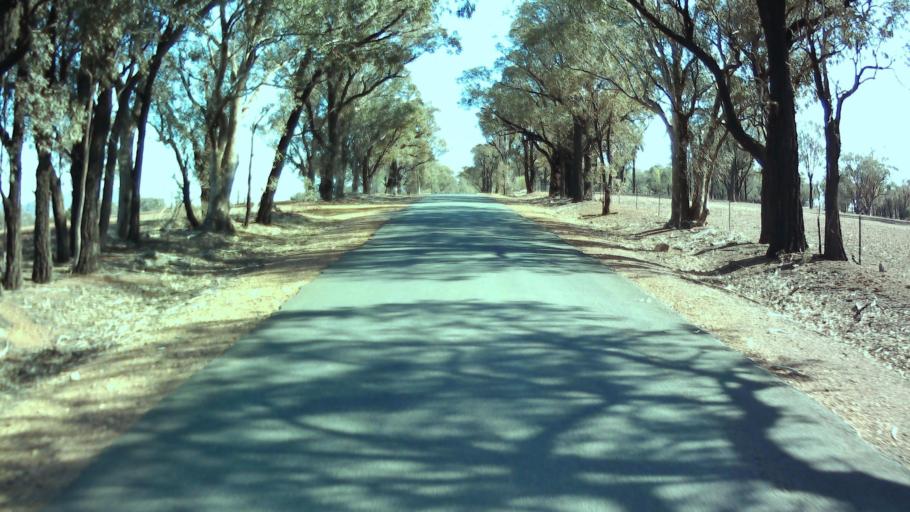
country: AU
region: New South Wales
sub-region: Weddin
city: Grenfell
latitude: -33.7878
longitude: 147.9580
